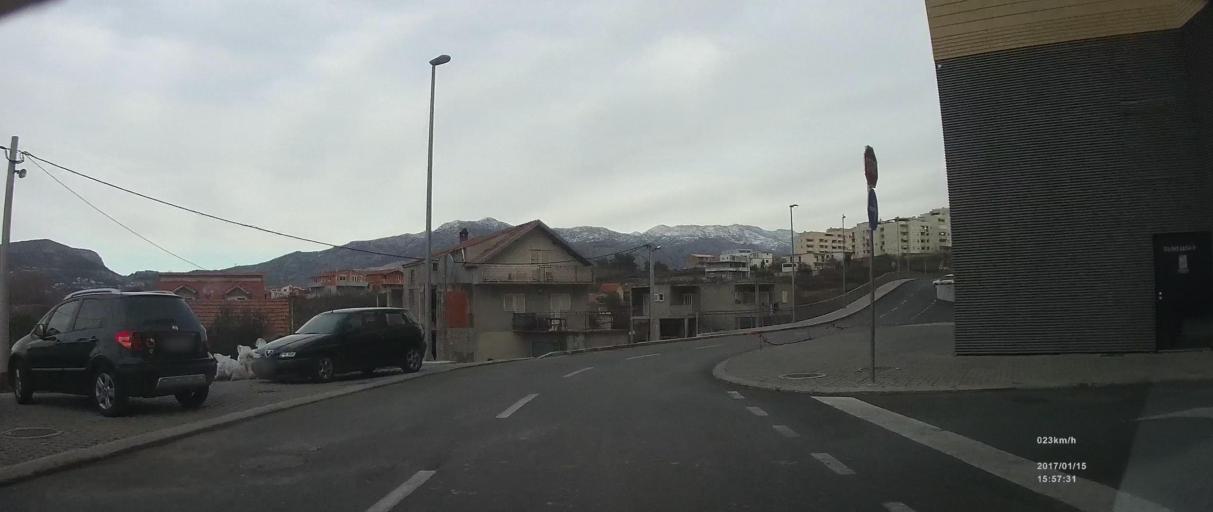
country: HR
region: Splitsko-Dalmatinska
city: Vranjic
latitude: 43.5199
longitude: 16.4840
